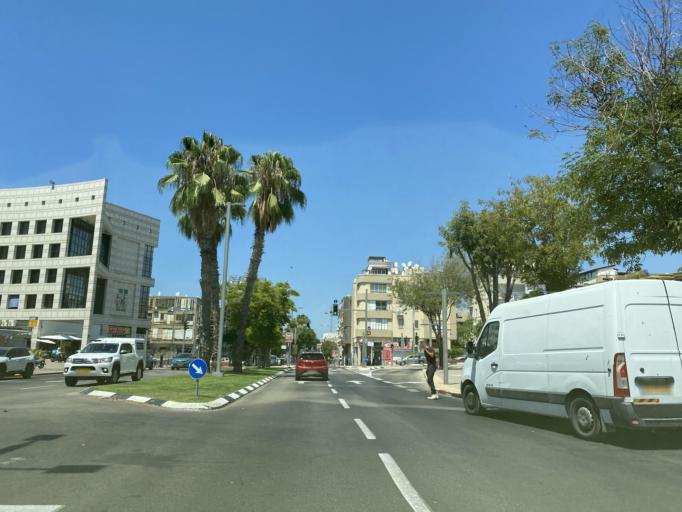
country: IL
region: Tel Aviv
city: Ramat HaSharon
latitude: 32.1622
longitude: 34.8426
